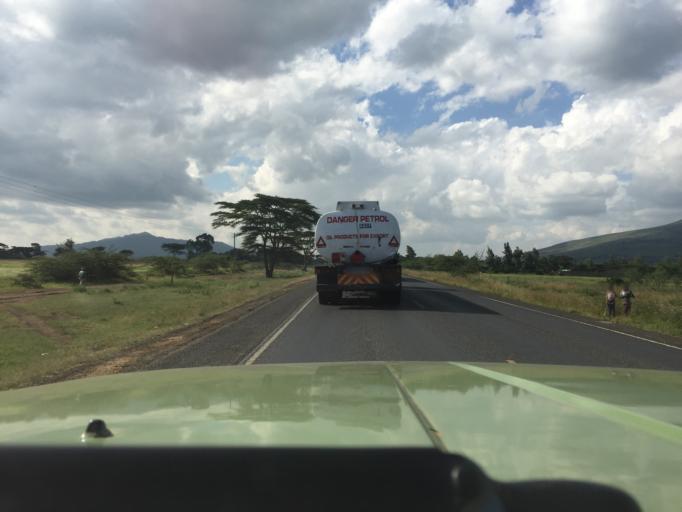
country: KE
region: Nakuru
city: Kijabe
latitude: -0.9602
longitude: 36.5592
